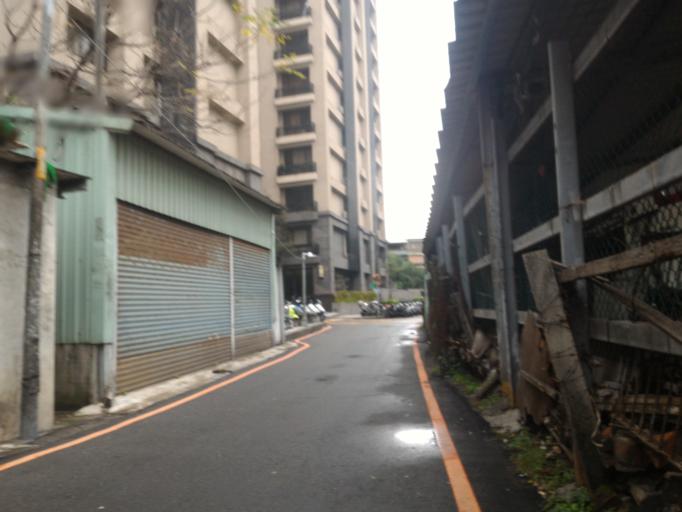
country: TW
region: Taipei
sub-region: Taipei
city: Banqiao
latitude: 25.0411
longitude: 121.4566
